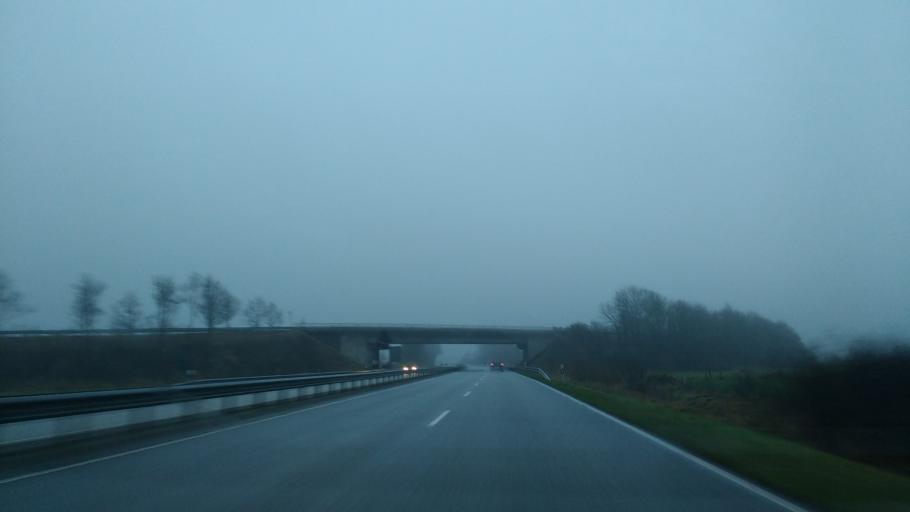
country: DE
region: Schleswig-Holstein
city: Jevenstedt
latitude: 54.2535
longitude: 9.6668
